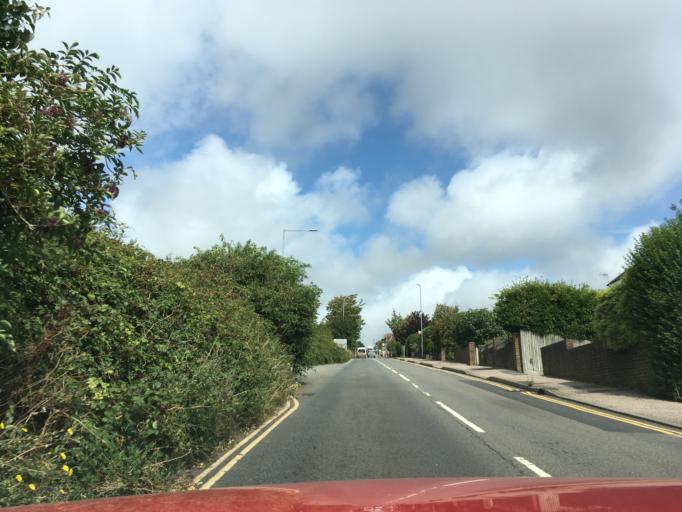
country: GB
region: England
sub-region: Brighton and Hove
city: Rottingdean
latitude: 50.8346
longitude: -0.0752
